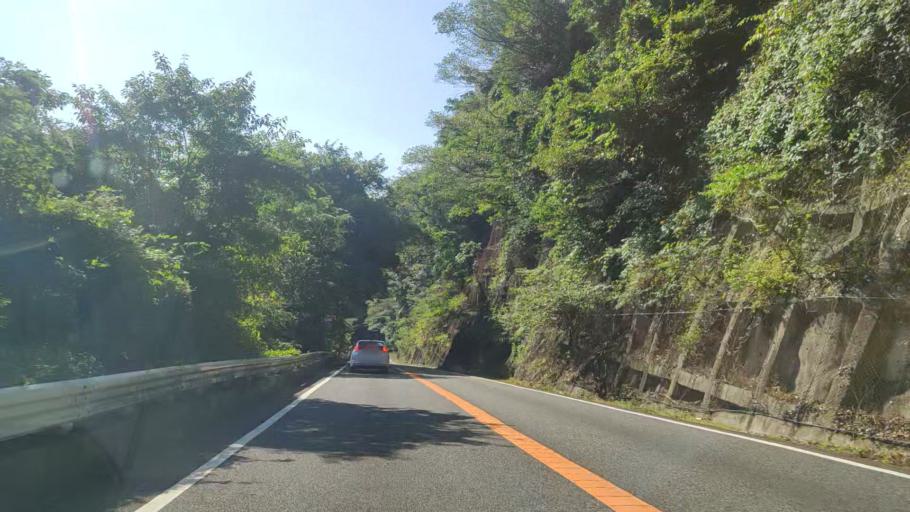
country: JP
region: Hyogo
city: Kobe
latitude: 34.6975
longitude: 135.1641
